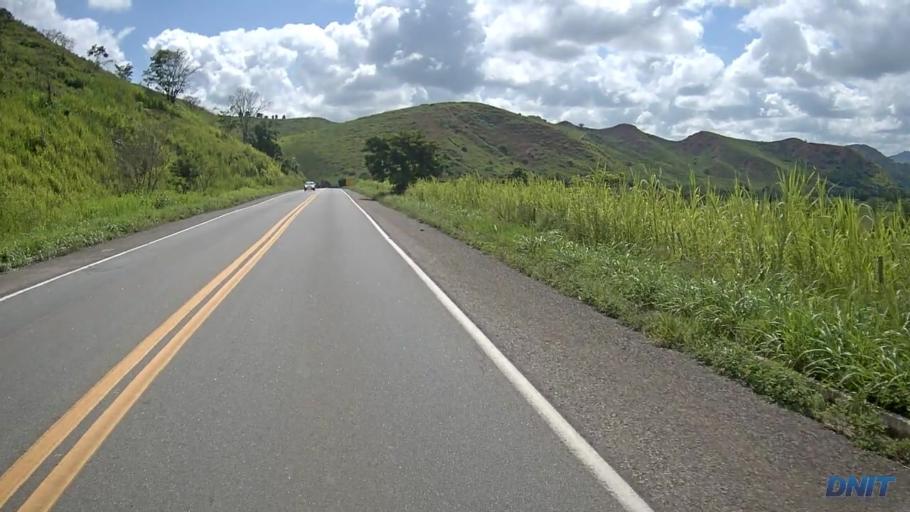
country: BR
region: Minas Gerais
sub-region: Belo Oriente
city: Belo Oriente
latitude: -19.1381
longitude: -42.2180
